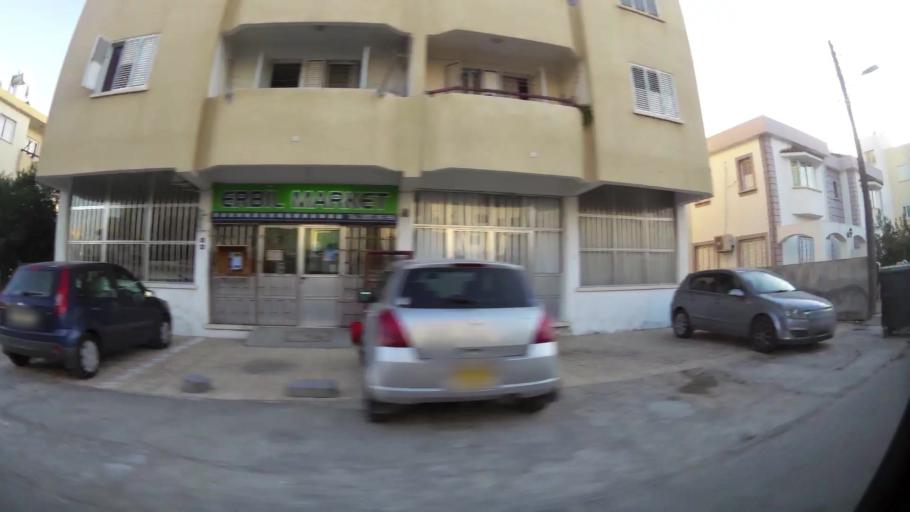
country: CY
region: Lefkosia
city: Nicosia
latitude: 35.2017
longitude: 33.3246
